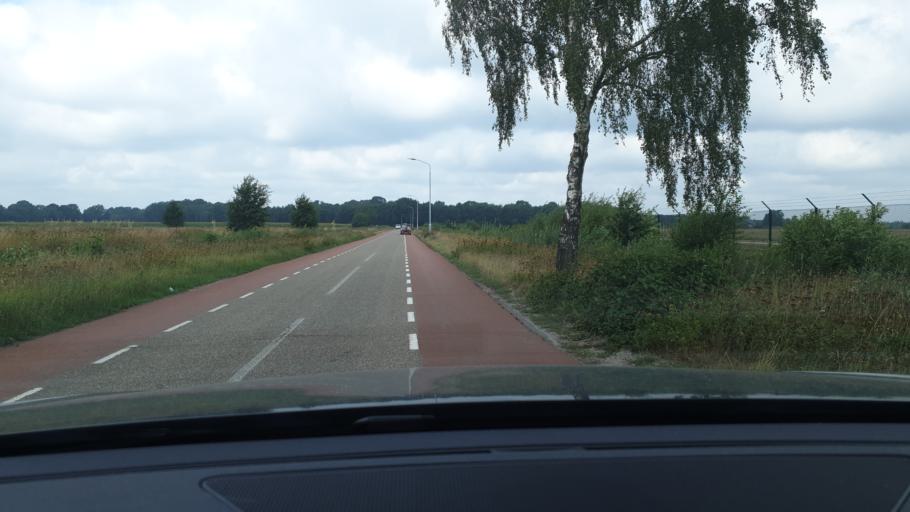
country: NL
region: North Brabant
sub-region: Gemeente Veldhoven
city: Oerle
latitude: 51.4363
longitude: 5.3623
